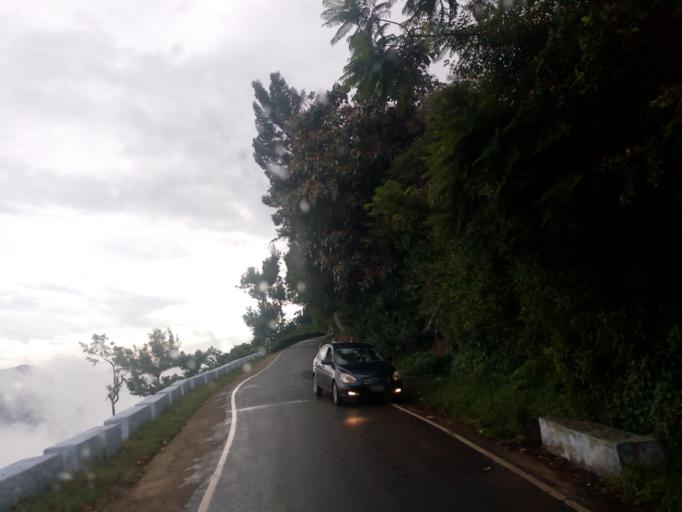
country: IN
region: Tamil Nadu
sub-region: Nilgiri
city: Kotagiri
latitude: 11.3631
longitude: 76.8500
